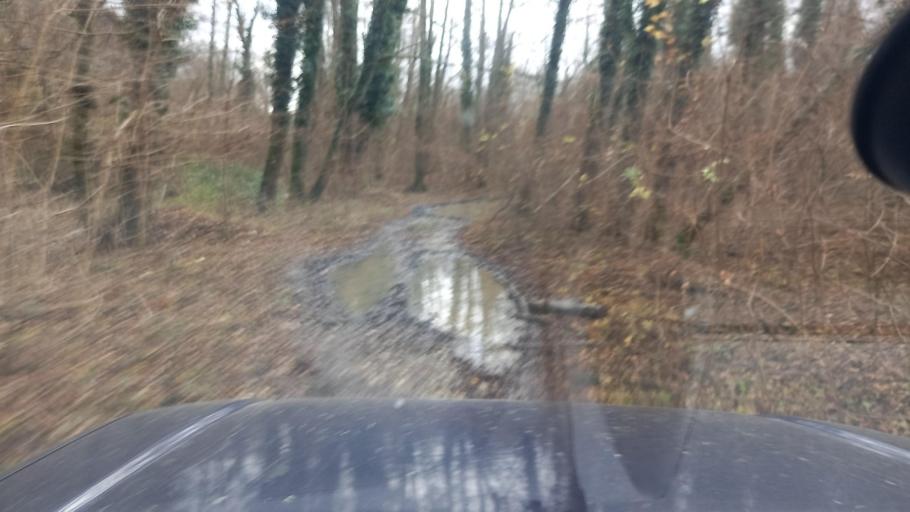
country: RU
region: Krasnodarskiy
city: Pshada
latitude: 44.4919
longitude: 38.4194
